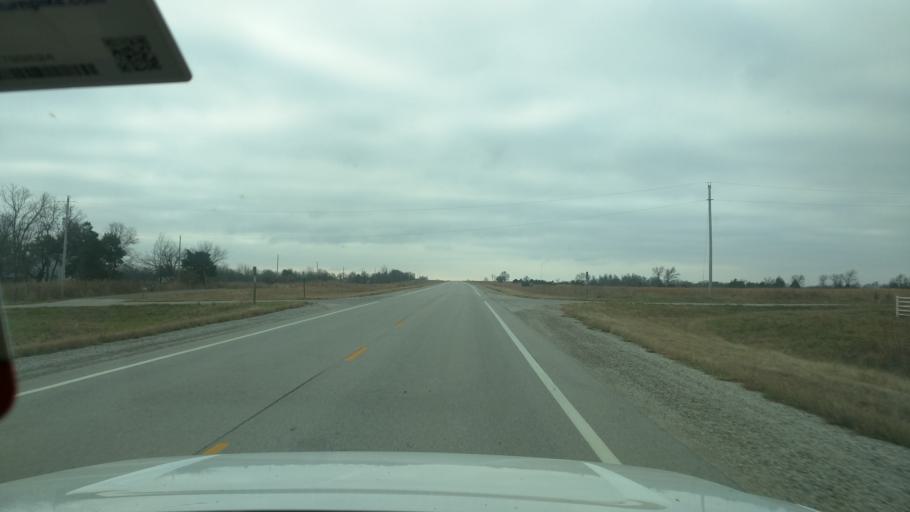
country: US
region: Kansas
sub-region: Elk County
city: Howard
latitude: 37.5776
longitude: -96.2534
